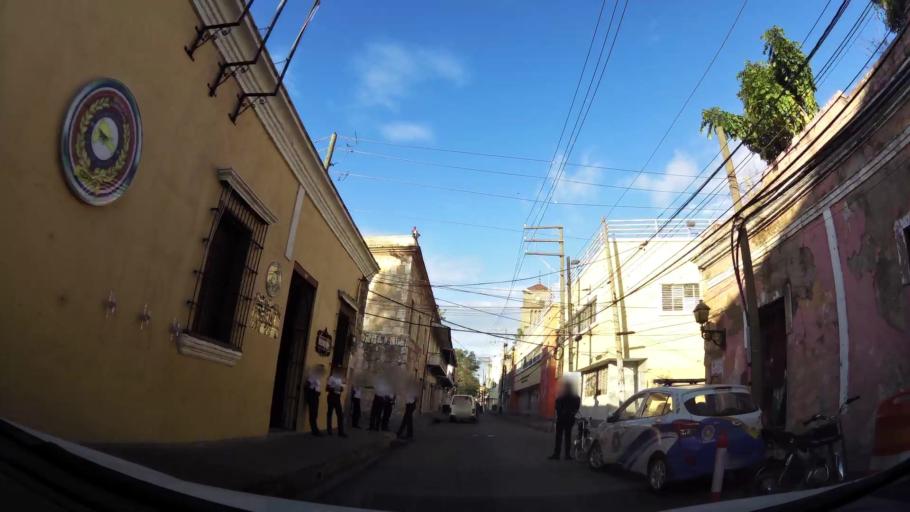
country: DO
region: Nacional
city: Ciudad Nueva
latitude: 18.4750
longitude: -69.8864
